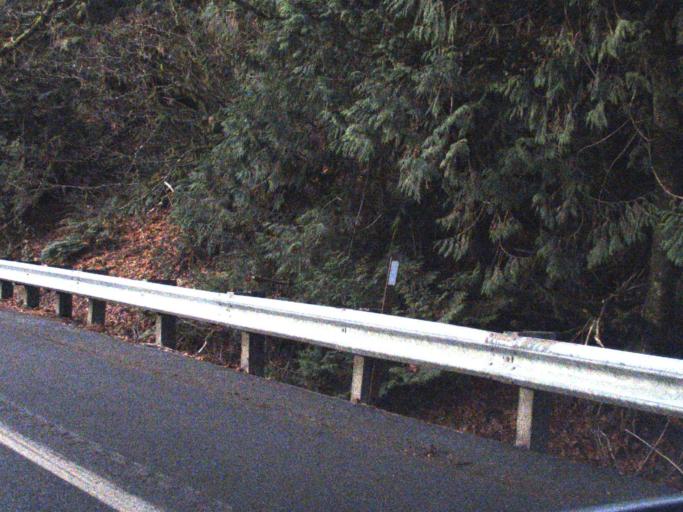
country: US
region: Washington
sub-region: Snohomish County
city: Darrington
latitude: 48.4879
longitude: -121.5989
